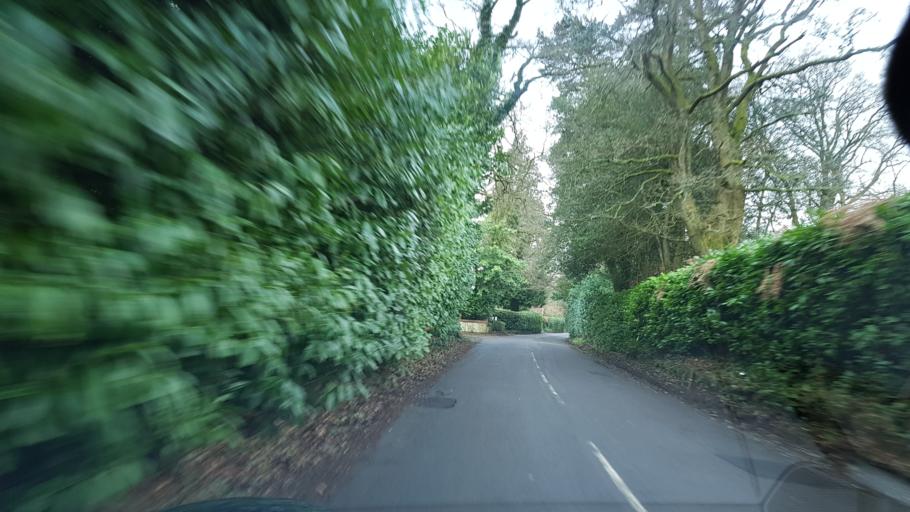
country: GB
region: England
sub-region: Surrey
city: Hindhead
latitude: 51.1035
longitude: -0.7420
